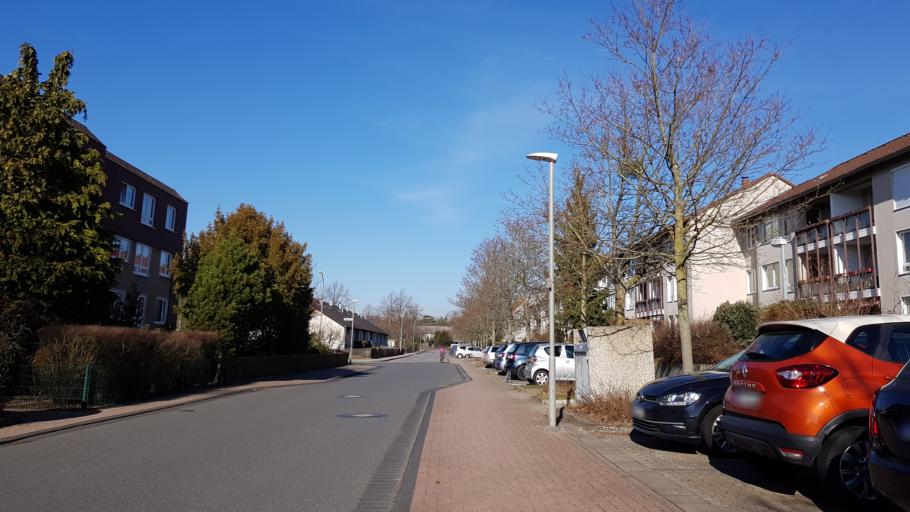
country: DE
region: Lower Saxony
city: Gifhorn
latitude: 52.4849
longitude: 10.5654
